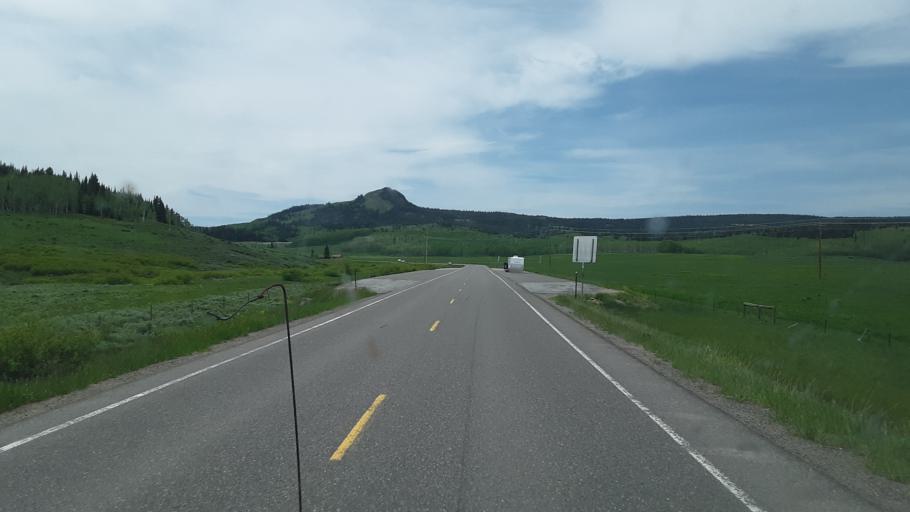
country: US
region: Colorado
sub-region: Routt County
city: Steamboat Springs
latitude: 40.3940
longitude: -106.5629
